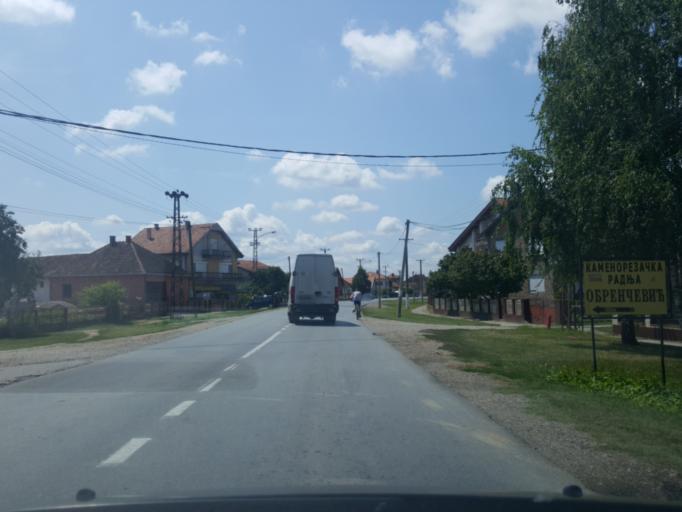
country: RS
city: Salas Nocajski
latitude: 44.9507
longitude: 19.5932
